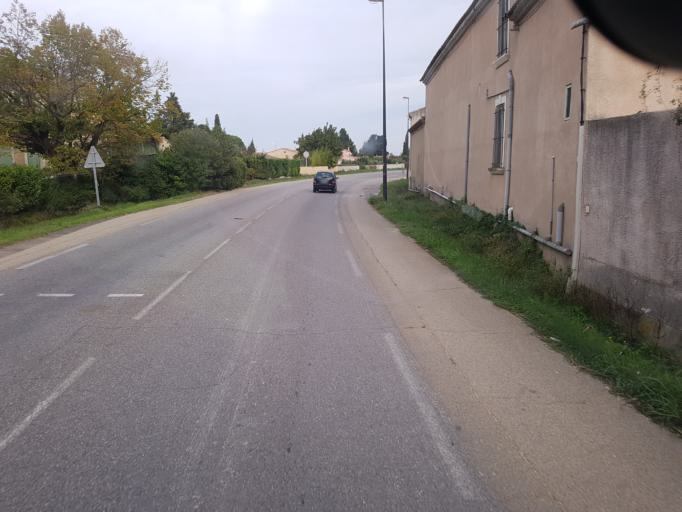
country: FR
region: Provence-Alpes-Cote d'Azur
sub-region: Departement des Bouches-du-Rhone
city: Barbentane
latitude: 43.9050
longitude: 4.7578
